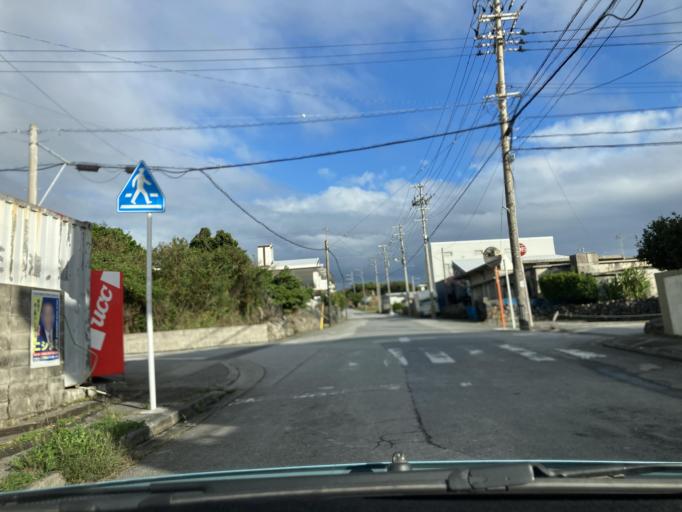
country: JP
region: Okinawa
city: Itoman
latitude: 26.1155
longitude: 127.6777
